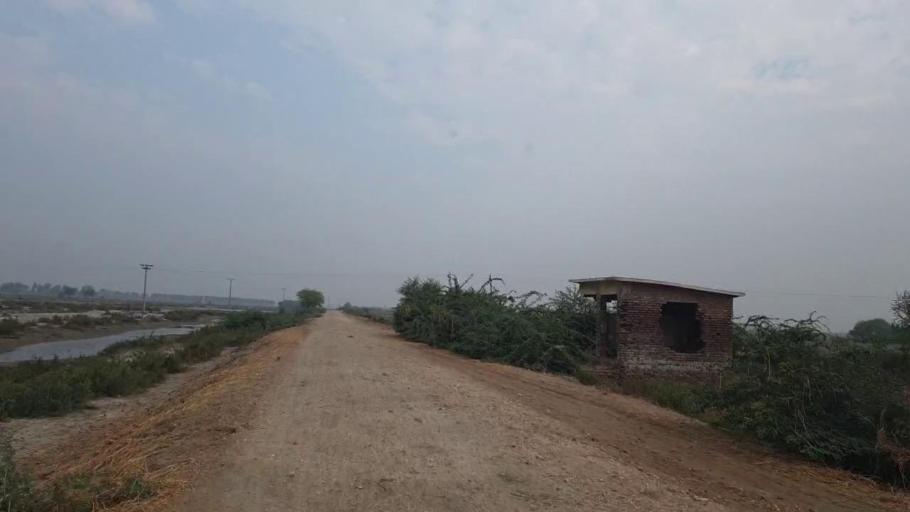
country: PK
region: Sindh
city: Talhar
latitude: 24.8146
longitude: 68.8765
